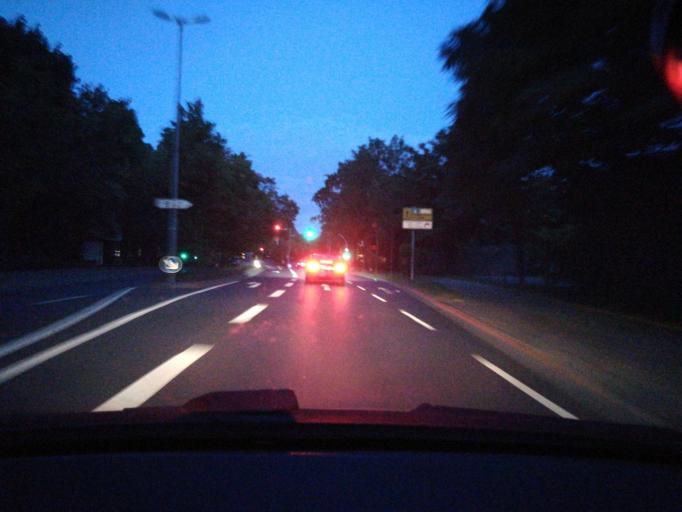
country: DE
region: North Rhine-Westphalia
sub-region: Regierungsbezirk Detmold
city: Minden
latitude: 52.2922
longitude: 8.9181
